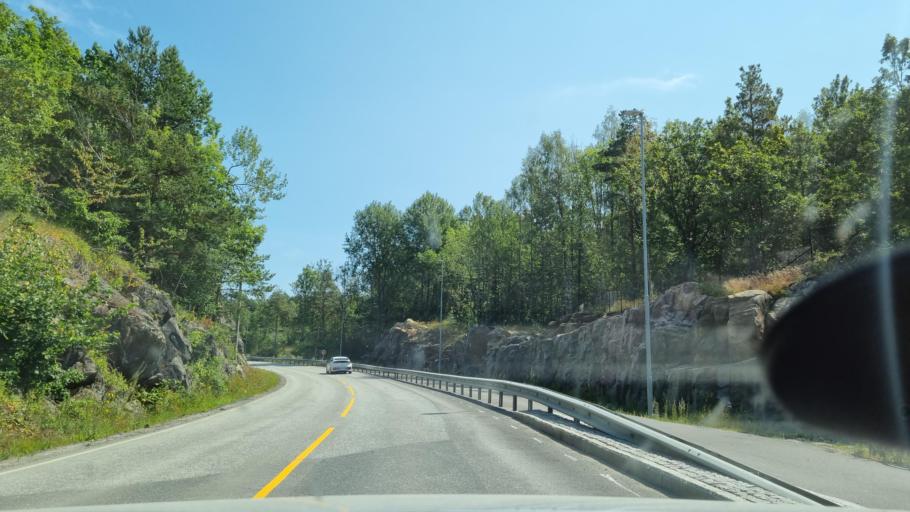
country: NO
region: Aust-Agder
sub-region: Arendal
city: Arendal
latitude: 58.4661
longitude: 8.8305
